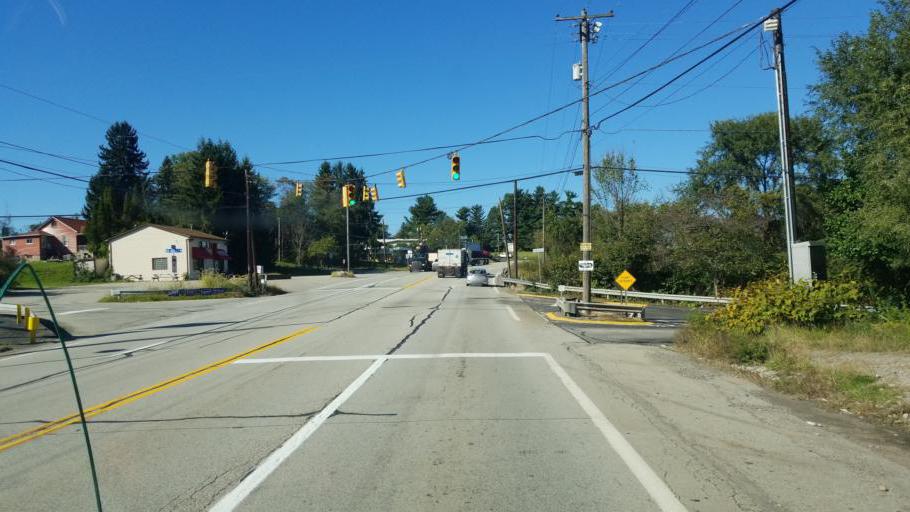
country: US
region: Pennsylvania
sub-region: Westmoreland County
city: Trafford
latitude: 40.3556
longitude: -79.7694
